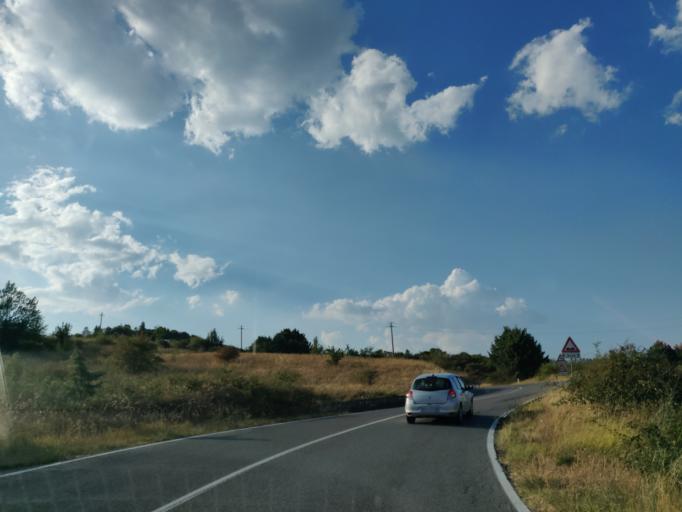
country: IT
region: Tuscany
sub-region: Provincia di Siena
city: Piancastagnaio
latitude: 42.8373
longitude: 11.7118
